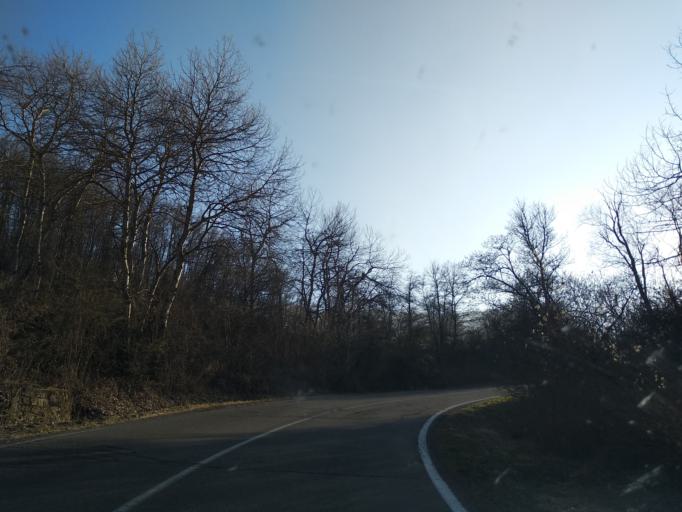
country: IT
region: Emilia-Romagna
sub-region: Provincia di Reggio Emilia
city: Busana
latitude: 44.4063
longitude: 10.3266
